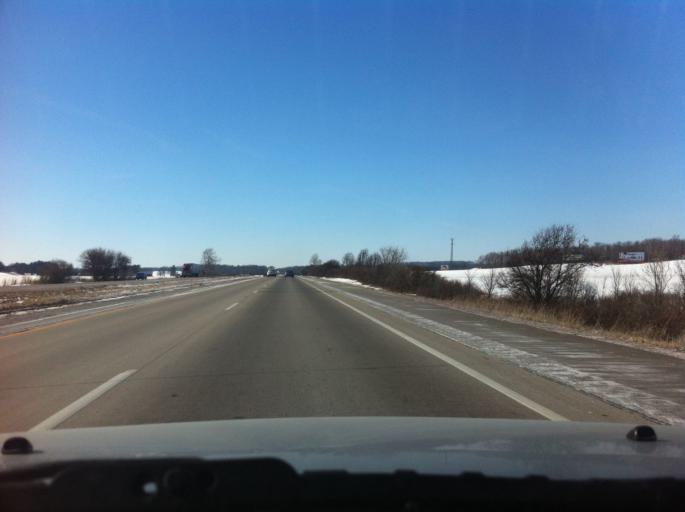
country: US
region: Wisconsin
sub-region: Sauk County
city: Baraboo
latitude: 43.5501
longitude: -89.6792
